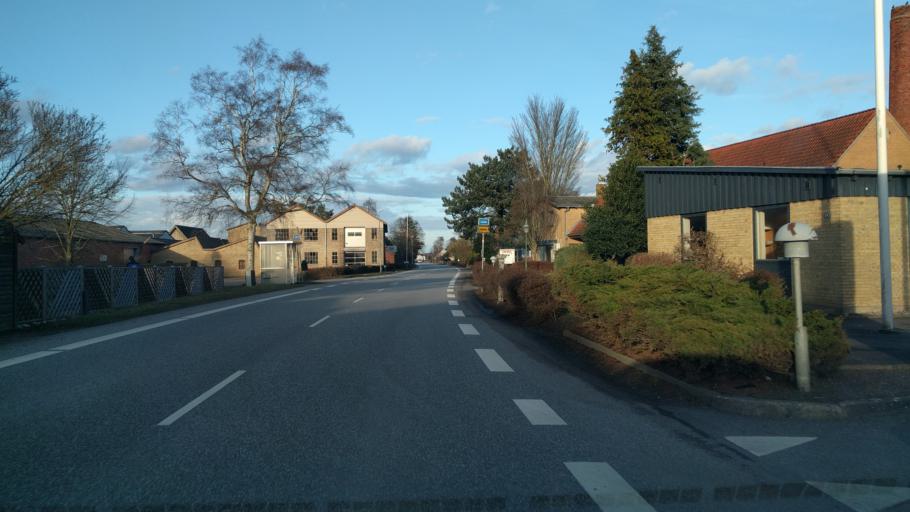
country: DK
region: South Denmark
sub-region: Kerteminde Kommune
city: Kerteminde
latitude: 55.4082
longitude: 10.6231
